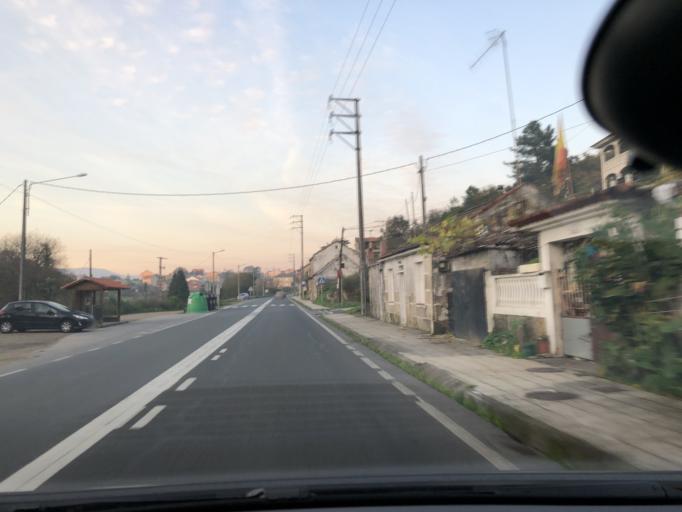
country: ES
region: Galicia
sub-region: Provincia de Pontevedra
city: Marin
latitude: 42.3813
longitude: -8.7162
